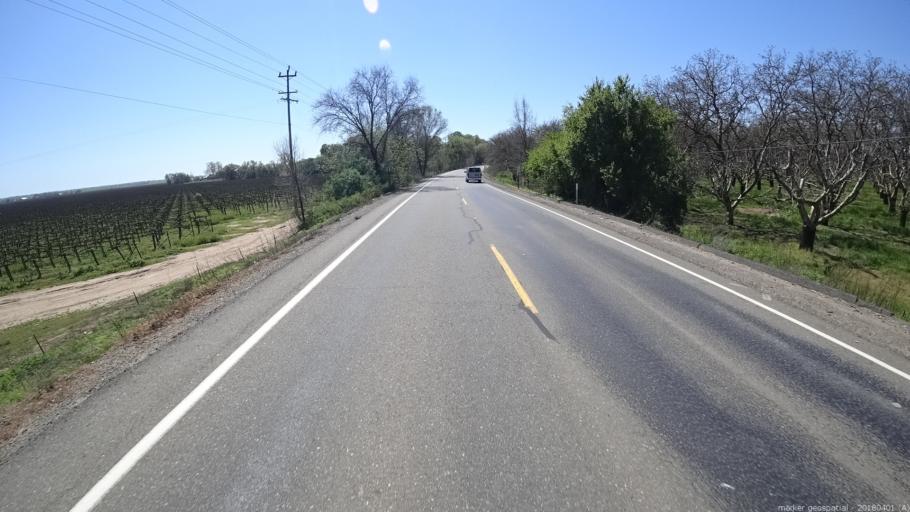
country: US
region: California
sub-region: Sacramento County
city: Rancho Murieta
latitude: 38.4904
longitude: -121.1618
